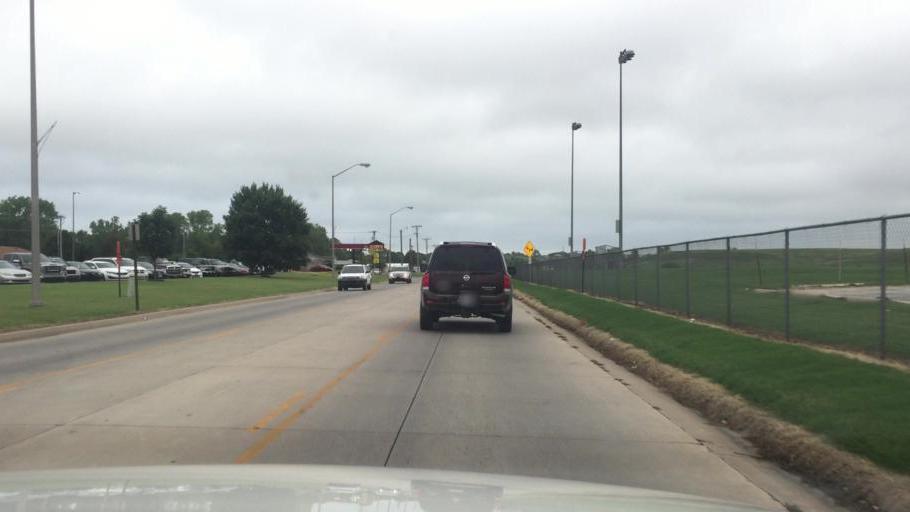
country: US
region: Kansas
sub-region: Montgomery County
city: Coffeyville
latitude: 37.0422
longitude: -95.6473
